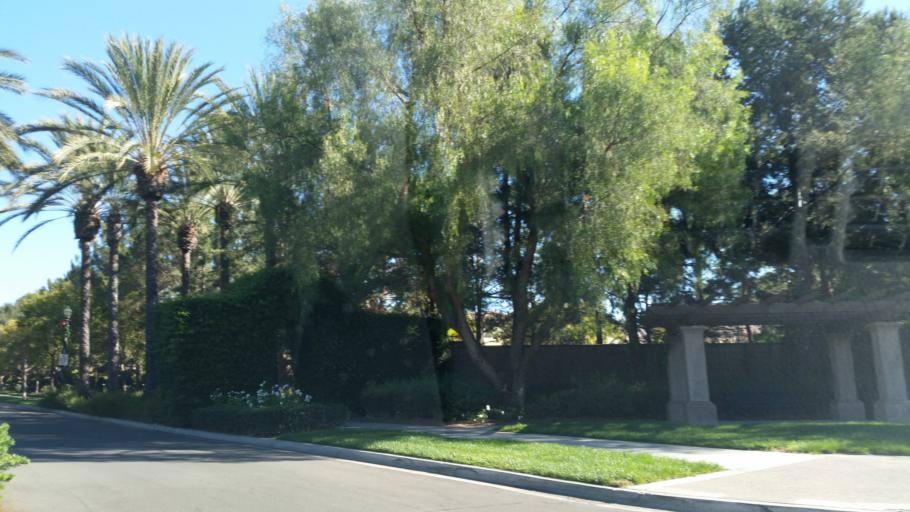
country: US
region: California
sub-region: Orange County
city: North Tustin
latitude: 33.7212
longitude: -117.7761
